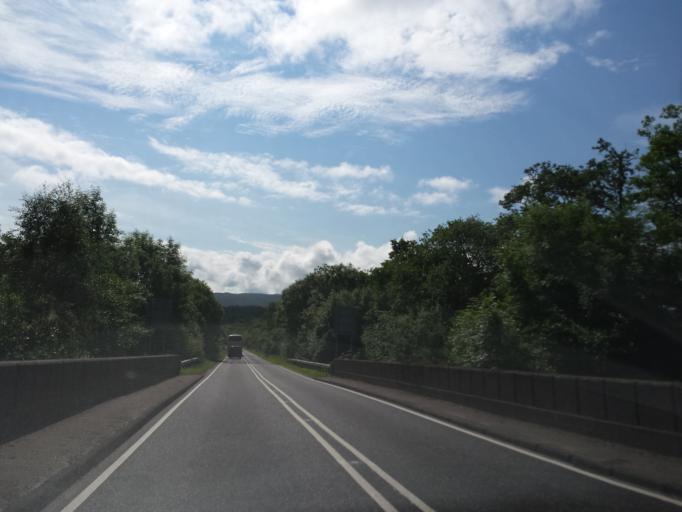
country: GB
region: Scotland
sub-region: Argyll and Bute
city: Garelochhead
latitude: 56.4085
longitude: -5.0191
